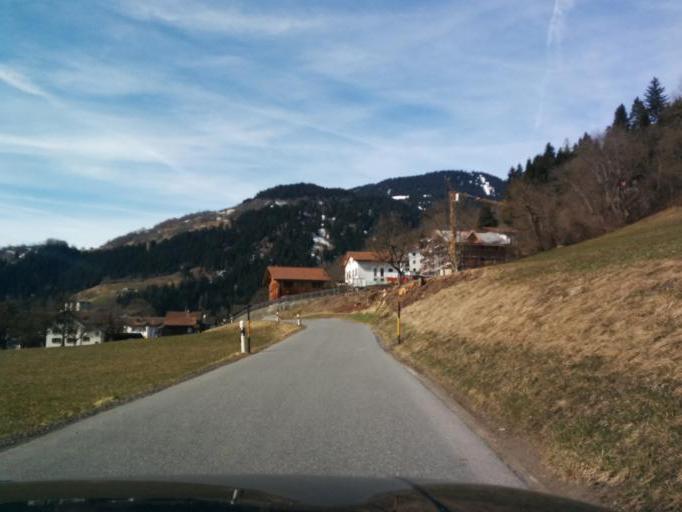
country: CH
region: Grisons
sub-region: Surselva District
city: Laax
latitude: 46.7888
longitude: 9.2374
